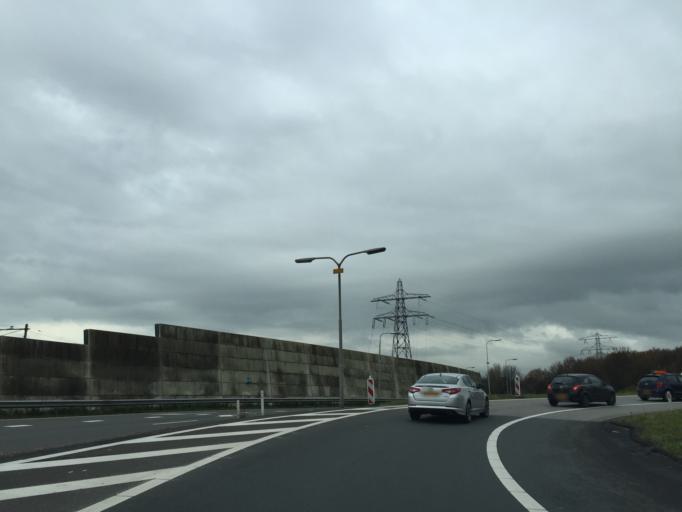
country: NL
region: South Holland
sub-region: Gemeente Schiedam
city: Schiedam
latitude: 51.9255
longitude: 4.4029
